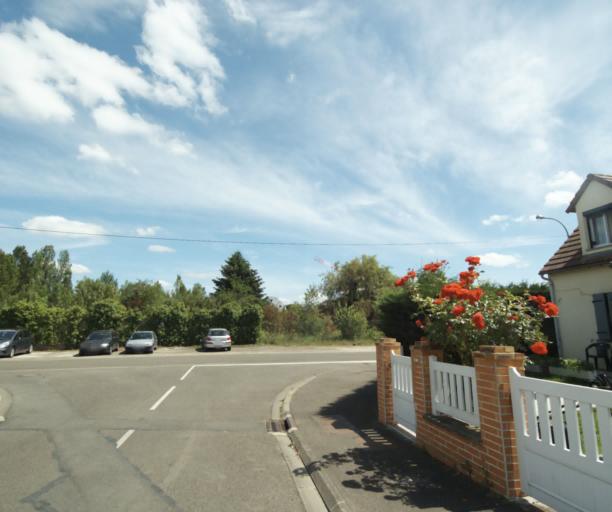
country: FR
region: Centre
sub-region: Departement d'Eure-et-Loir
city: Luce
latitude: 48.4373
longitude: 1.4679
